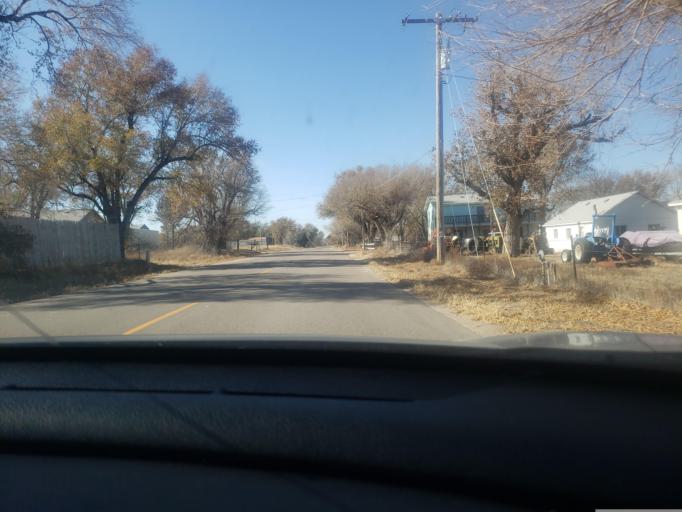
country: US
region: Kansas
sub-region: Finney County
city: Garden City
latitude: 37.9512
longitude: -100.8655
